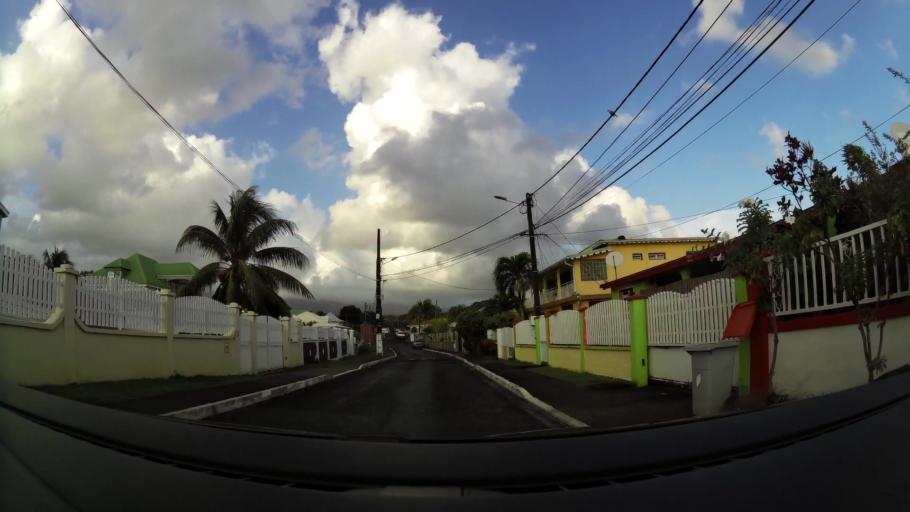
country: GP
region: Guadeloupe
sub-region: Guadeloupe
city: Petit-Bourg
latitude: 16.1336
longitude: -61.5768
